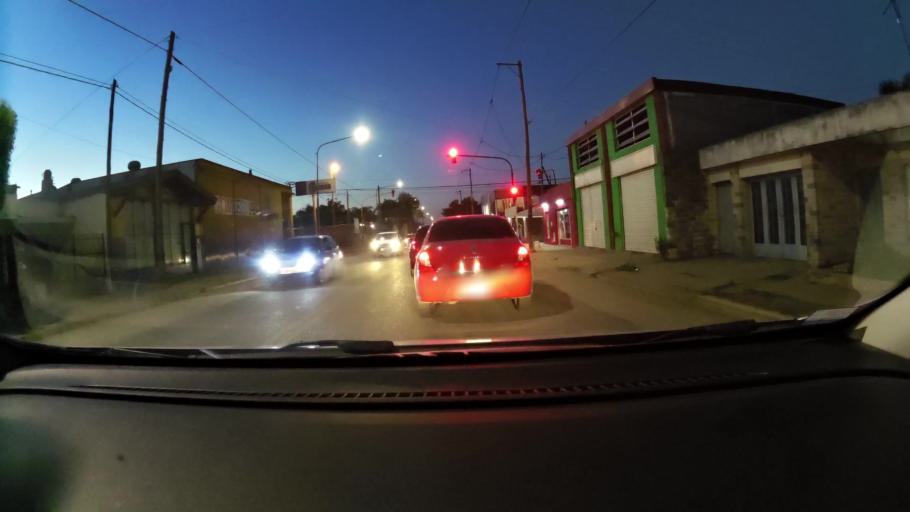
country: AR
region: Cordoba
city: Villa Maria
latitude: -32.4002
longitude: -63.2327
